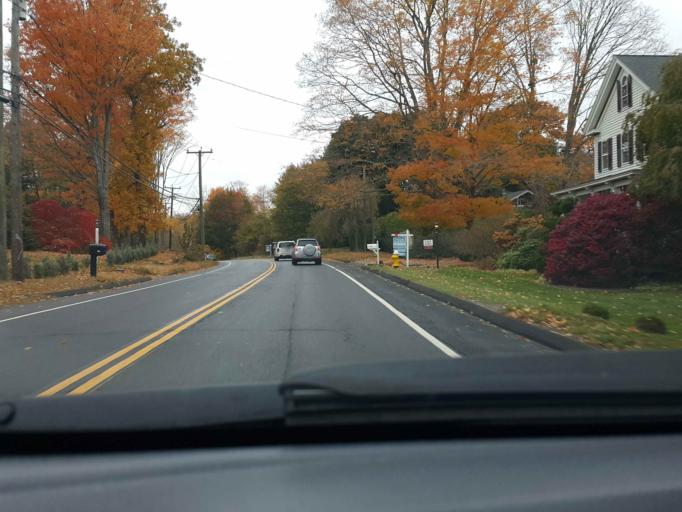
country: US
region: Connecticut
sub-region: New Haven County
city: Madison Center
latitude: 41.2847
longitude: -72.6371
